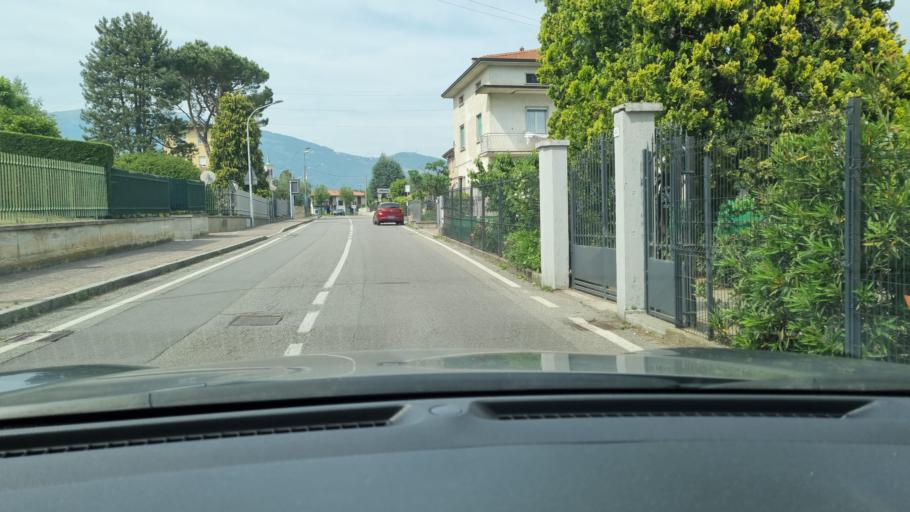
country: IT
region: Lombardy
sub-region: Provincia di Bergamo
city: Ambivere
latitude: 45.7137
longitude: 9.5481
